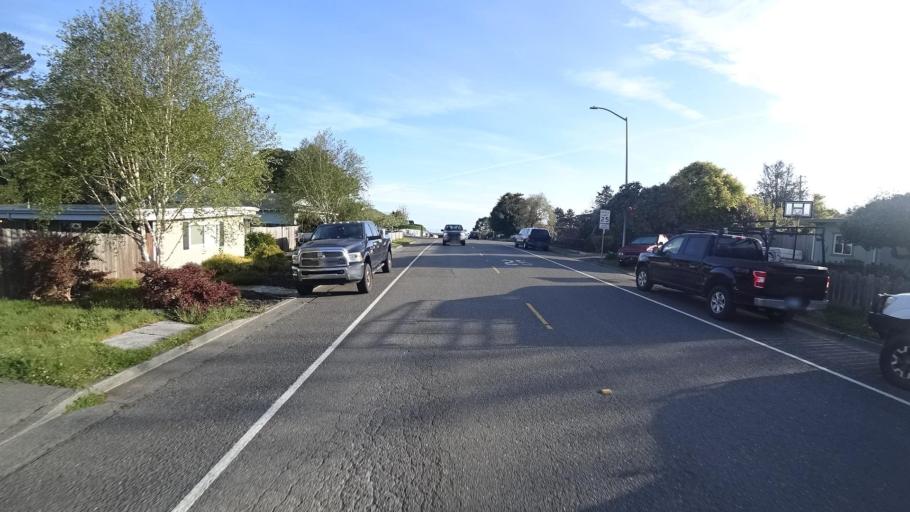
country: US
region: California
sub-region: Humboldt County
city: Humboldt Hill
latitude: 40.7182
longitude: -124.2033
